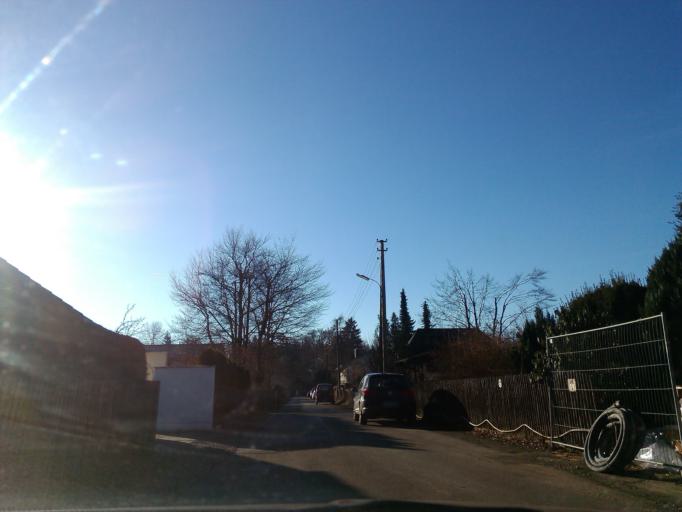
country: DE
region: Bavaria
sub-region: Upper Bavaria
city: Gauting
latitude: 48.0529
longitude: 11.3618
